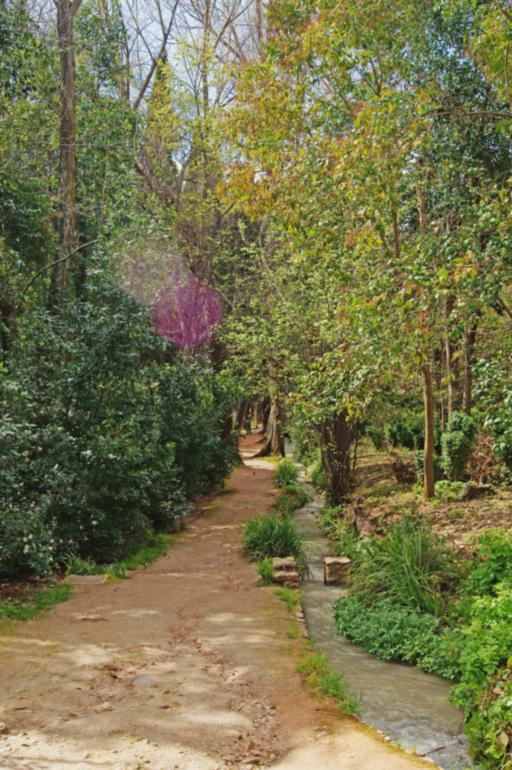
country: ES
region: Andalusia
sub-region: Provincia de Granada
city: Granada
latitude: 37.1778
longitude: -3.5845
